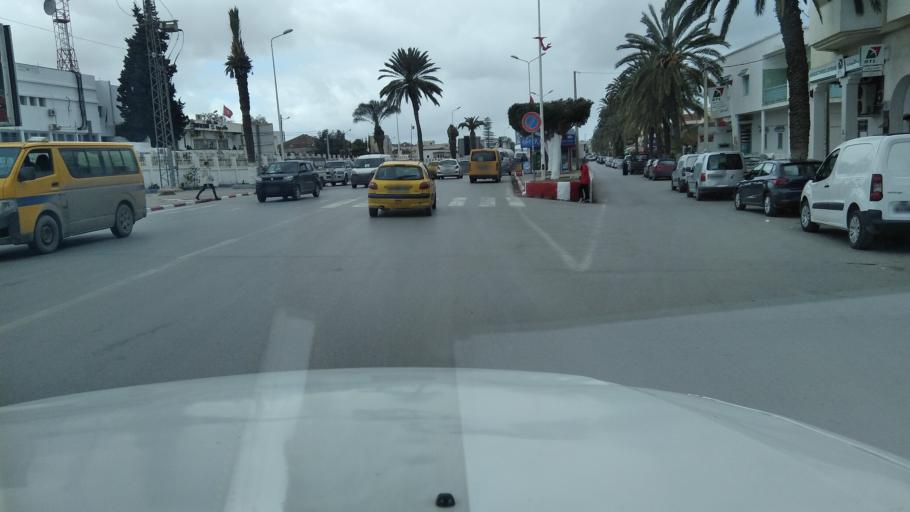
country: TN
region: Bin 'Arus
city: Ben Arous
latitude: 36.7520
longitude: 10.2244
